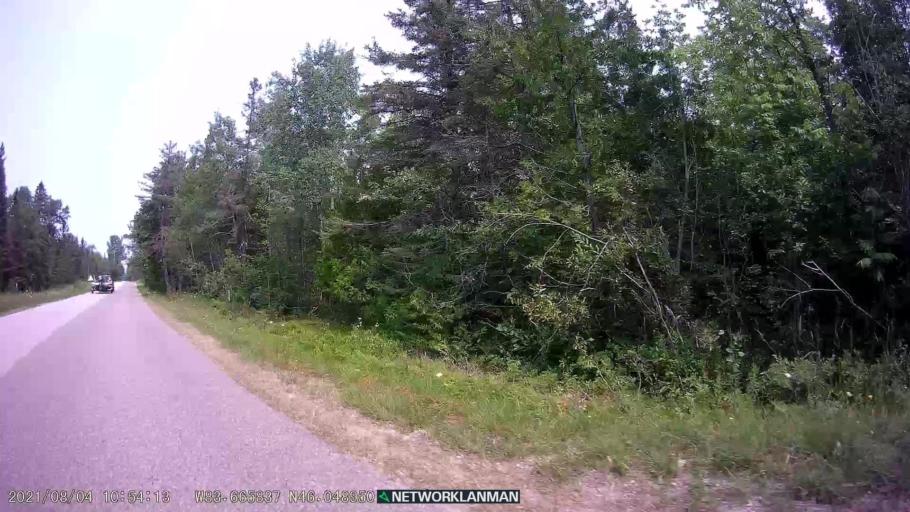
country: CA
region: Ontario
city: Thessalon
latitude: 46.0495
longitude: -83.6658
